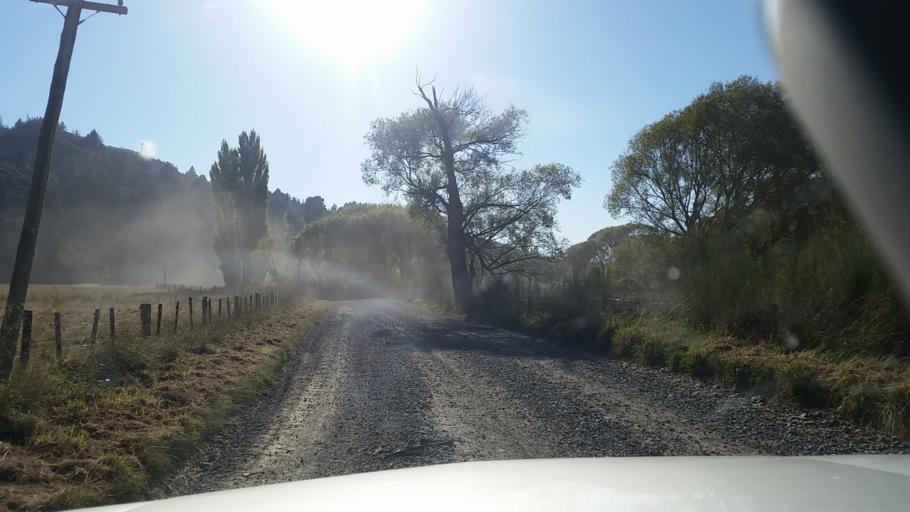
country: NZ
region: Marlborough
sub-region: Marlborough District
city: Blenheim
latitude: -41.4498
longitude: 173.8755
